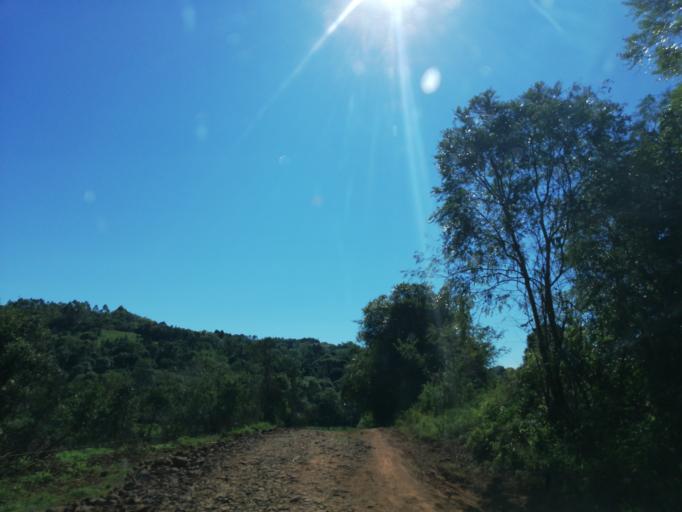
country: AR
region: Misiones
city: El Soberbio
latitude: -27.0662
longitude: -54.3865
